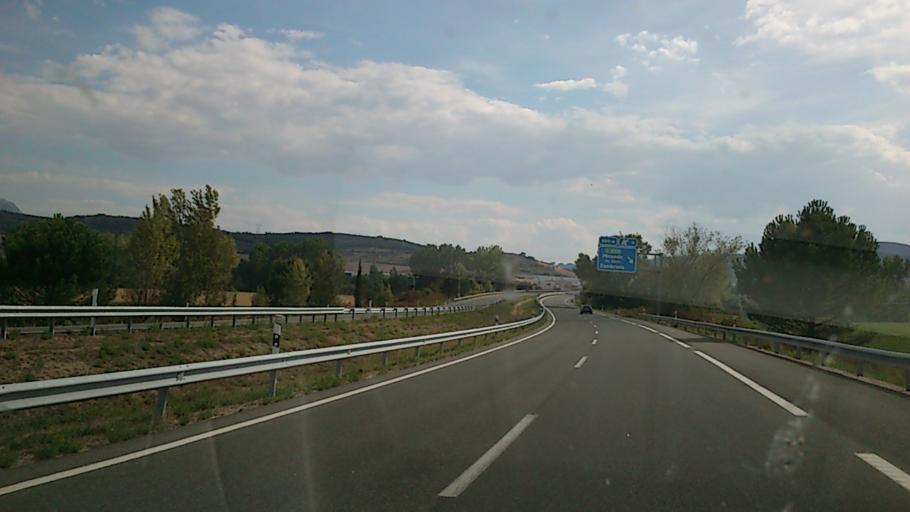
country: ES
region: Basque Country
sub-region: Provincia de Alava
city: Zambrana
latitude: 42.6855
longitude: -2.8916
